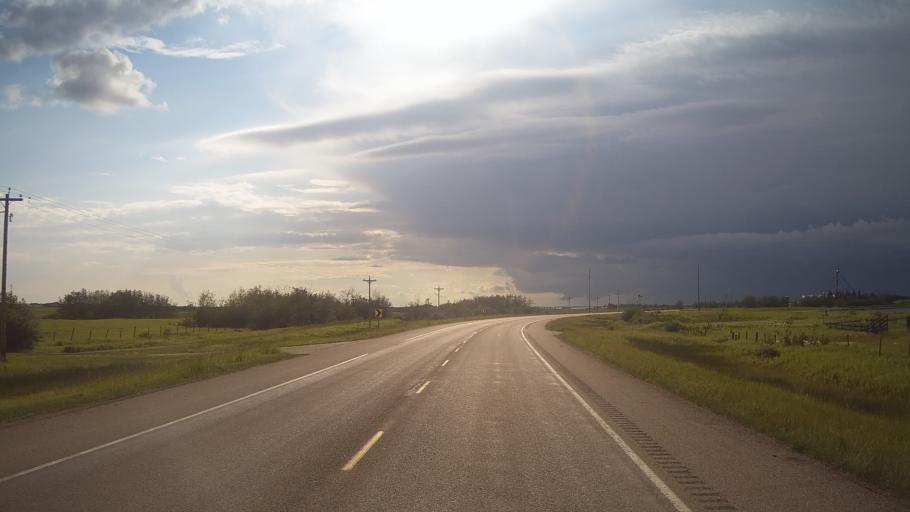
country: CA
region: Alberta
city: Vegreville
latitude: 53.2217
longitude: -112.2150
